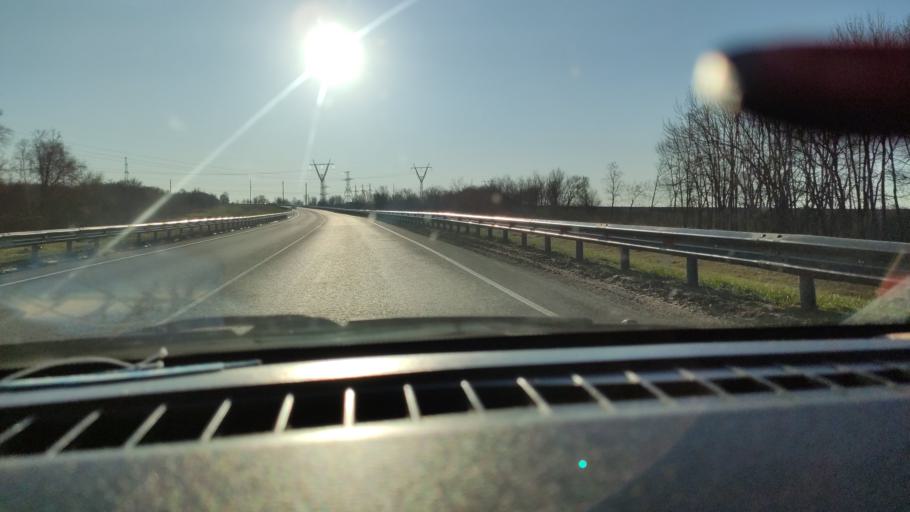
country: RU
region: Saratov
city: Tersa
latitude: 52.0832
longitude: 47.6673
